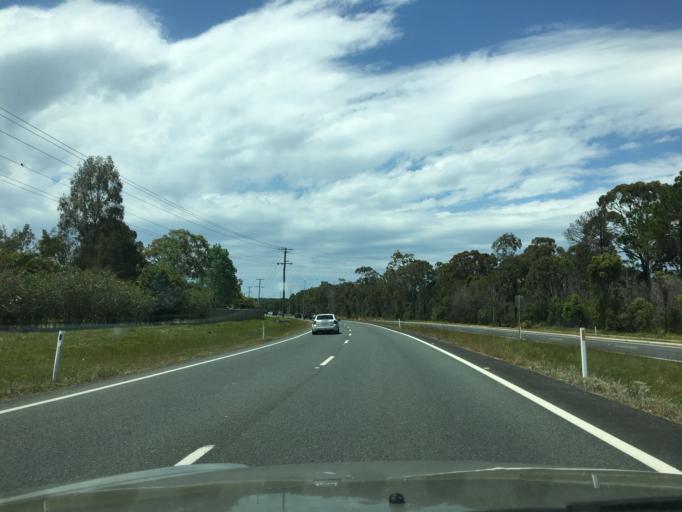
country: AU
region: Queensland
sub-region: Moreton Bay
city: Bongaree
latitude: -27.0653
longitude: 153.0689
